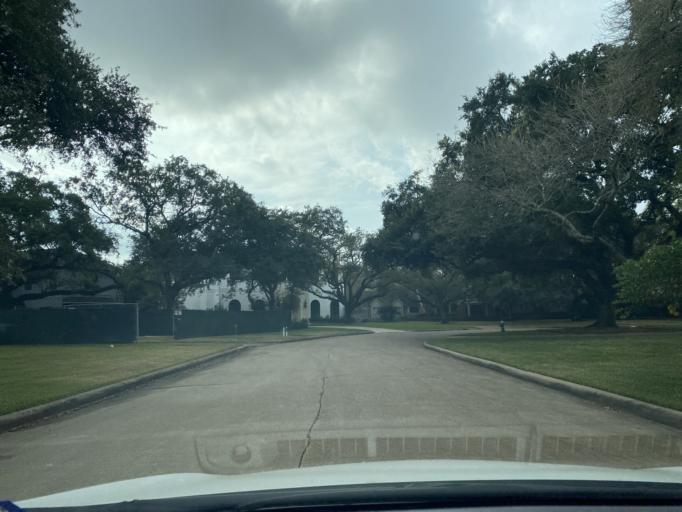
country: US
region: Texas
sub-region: Harris County
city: Hunters Creek Village
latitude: 29.7650
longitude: -95.4766
